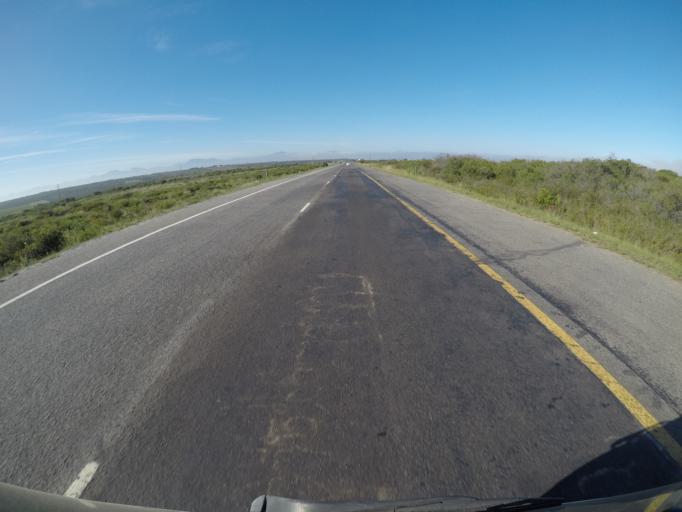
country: ZA
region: Western Cape
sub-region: Eden District Municipality
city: Mossel Bay
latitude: -34.1809
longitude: 22.0613
